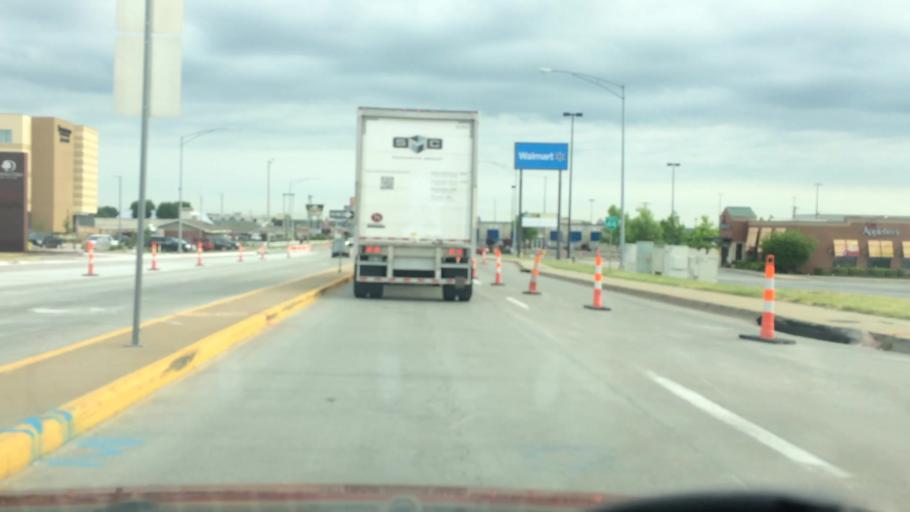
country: US
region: Missouri
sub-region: Greene County
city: Springfield
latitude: 37.2404
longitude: -93.2609
